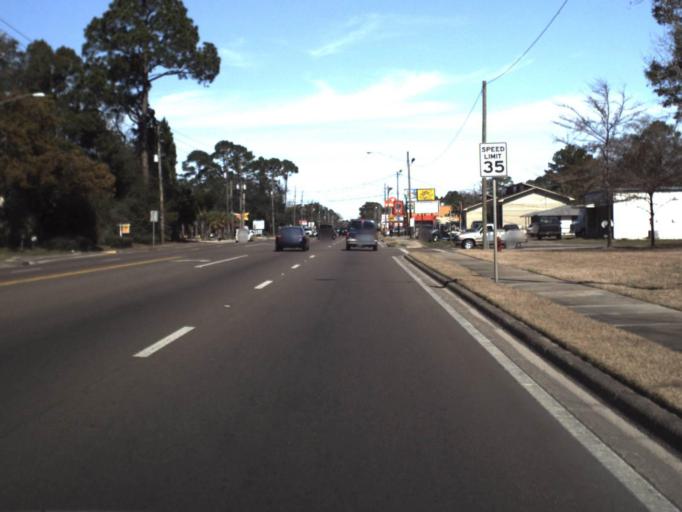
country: US
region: Florida
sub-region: Bay County
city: Lynn Haven
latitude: 30.2340
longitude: -85.6488
